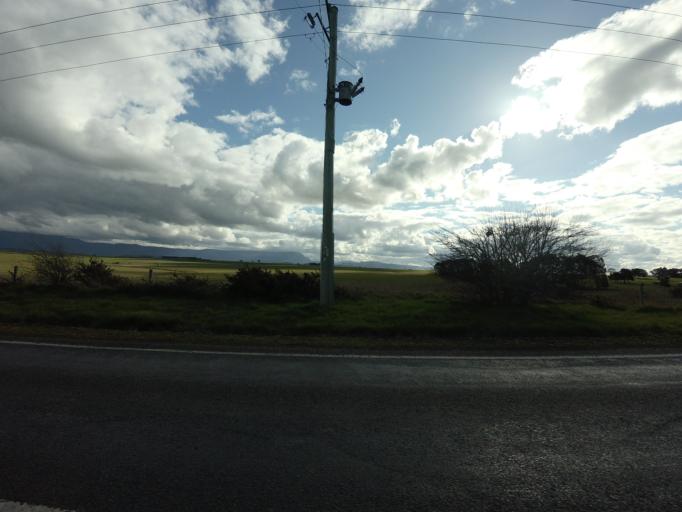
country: AU
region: Tasmania
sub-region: Northern Midlands
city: Longford
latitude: -41.6971
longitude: 147.0779
